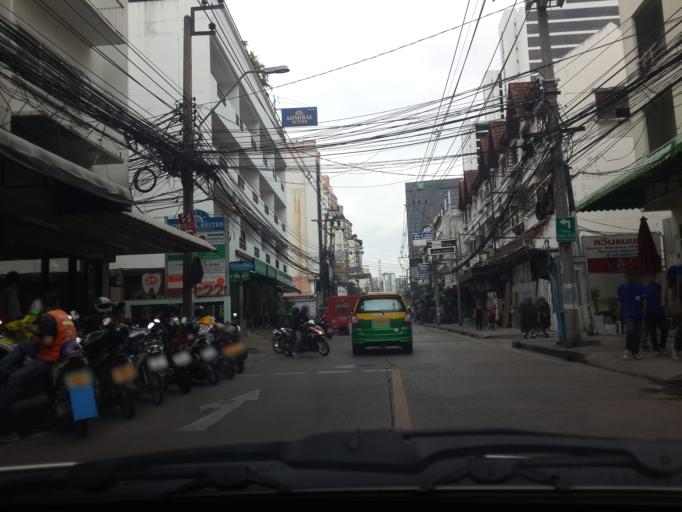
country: TH
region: Bangkok
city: Khlong Toei
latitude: 13.7287
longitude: 100.5651
